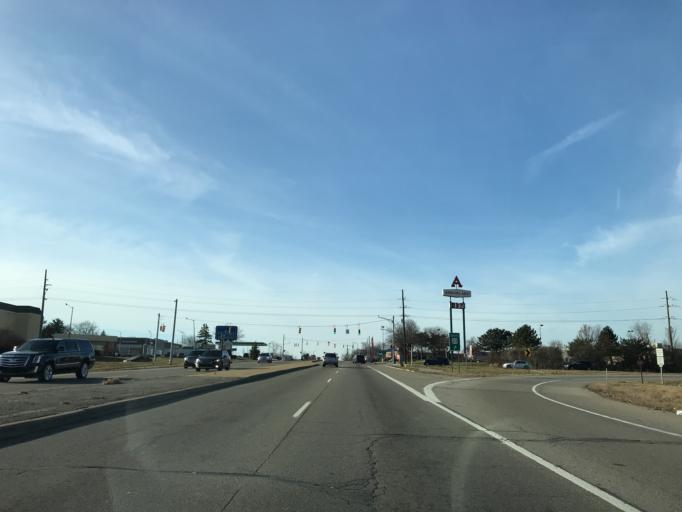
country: US
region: Michigan
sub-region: Washtenaw County
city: Ann Arbor
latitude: 42.2549
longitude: -83.6850
